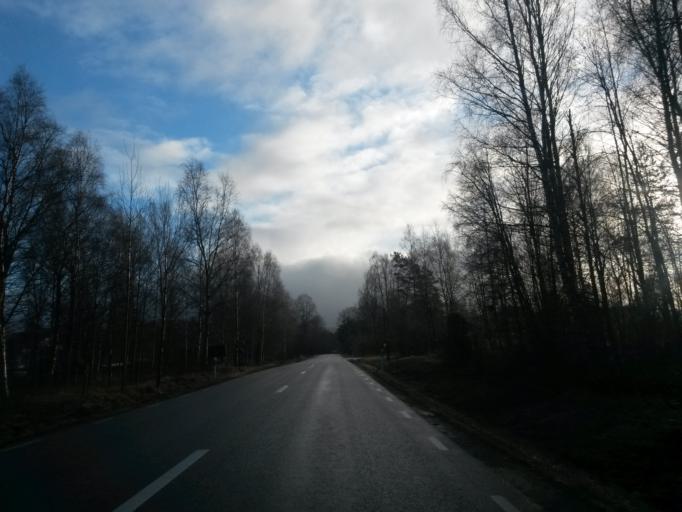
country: SE
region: Vaestra Goetaland
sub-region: Boras Kommun
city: Boras
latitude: 57.8310
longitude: 12.9944
